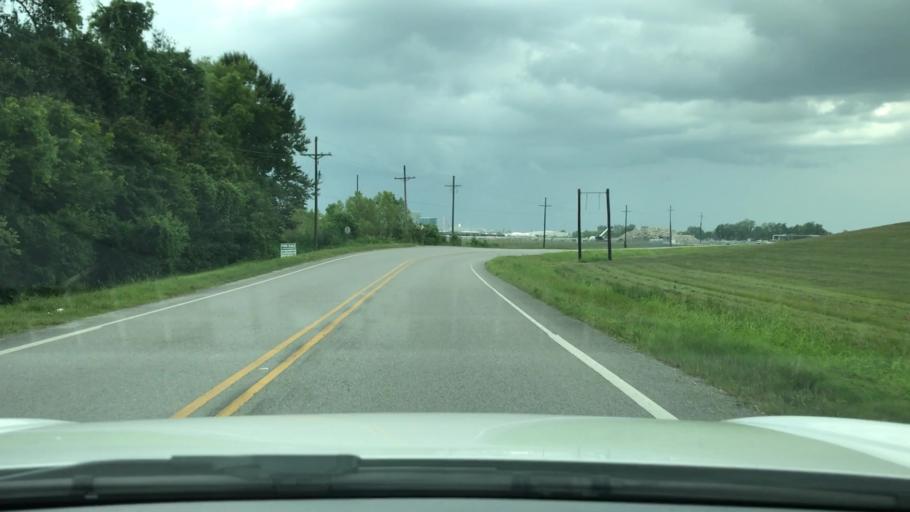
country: US
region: Louisiana
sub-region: Iberville Parish
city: Saint Gabriel
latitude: 30.2734
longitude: -91.1627
